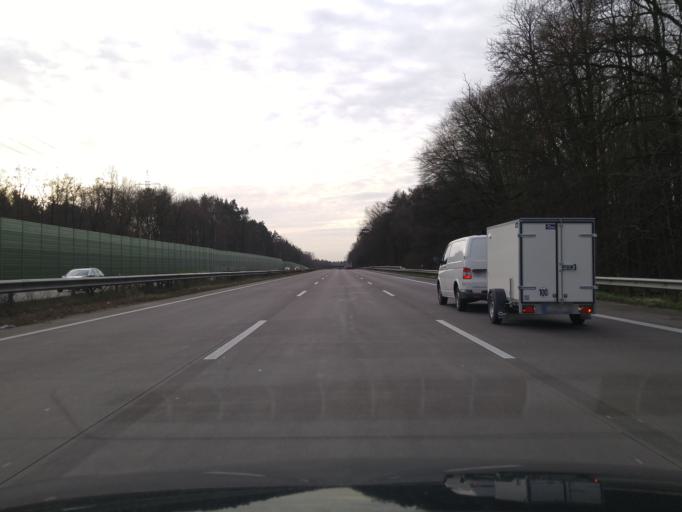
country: DE
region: Schleswig-Holstein
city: Grosshansdorf
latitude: 53.6654
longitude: 10.3025
